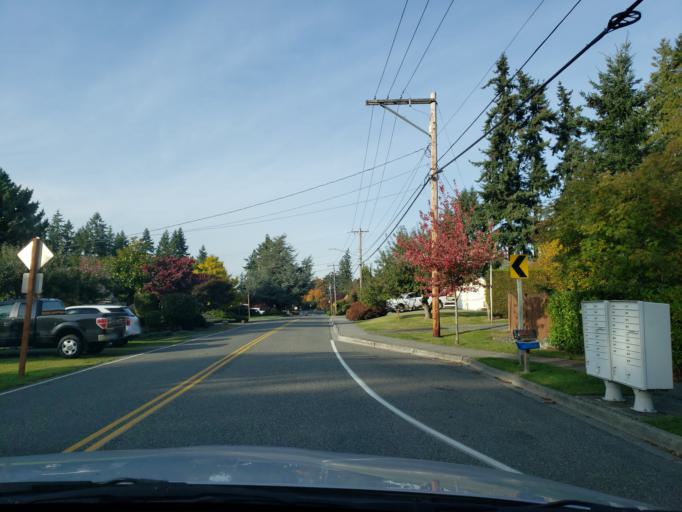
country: US
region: Washington
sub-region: Snohomish County
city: Mukilteo
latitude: 47.9361
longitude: -122.3011
